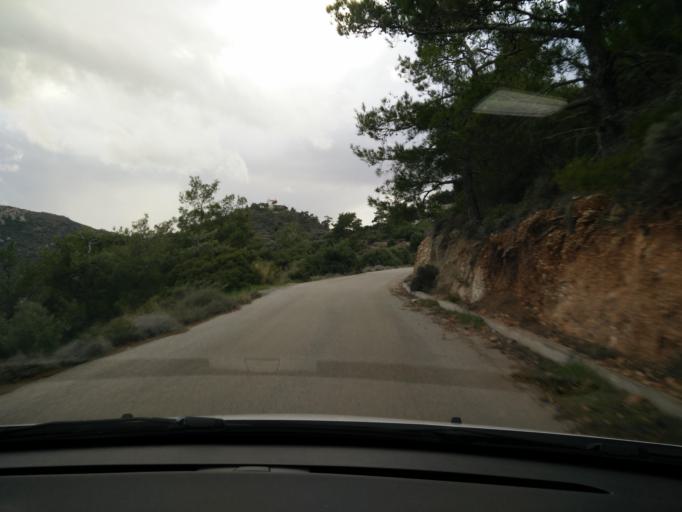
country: GR
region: Crete
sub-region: Nomos Lasithiou
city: Kritsa
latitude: 35.0987
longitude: 25.6920
